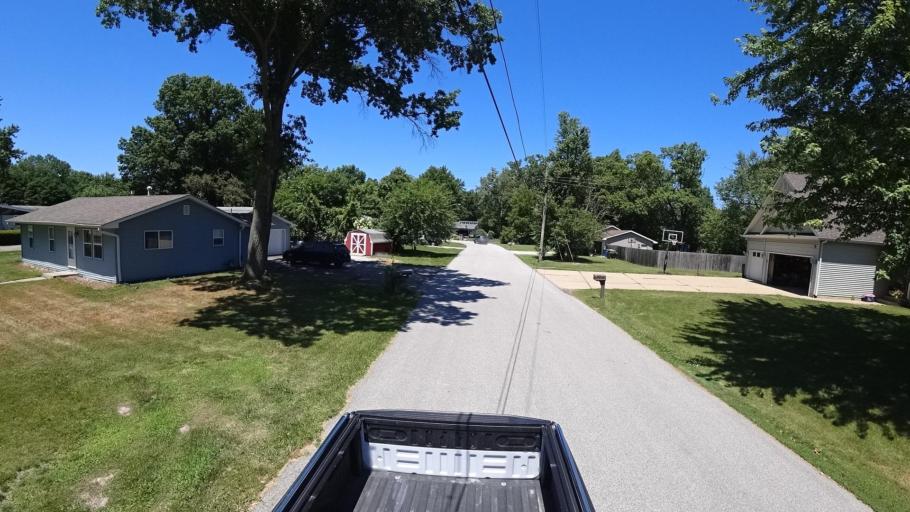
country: US
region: Indiana
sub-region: Porter County
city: Chesterton
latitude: 41.6177
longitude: -87.0540
